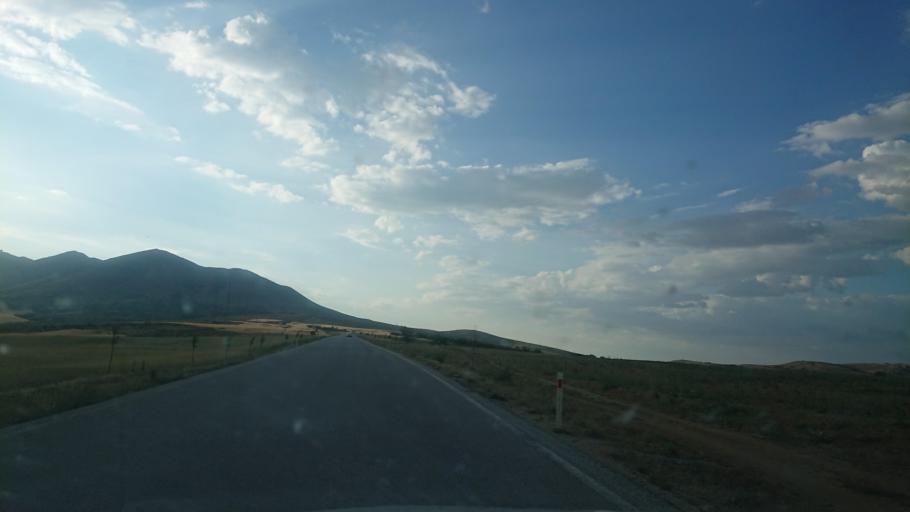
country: TR
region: Aksaray
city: Balci
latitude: 38.6131
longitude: 34.1012
